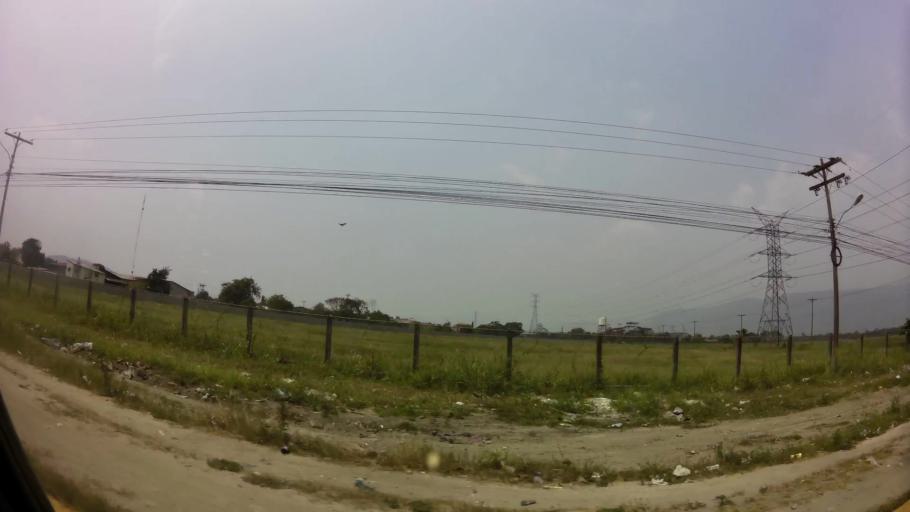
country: HN
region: Cortes
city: San Pedro Sula
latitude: 15.4785
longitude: -88.0021
